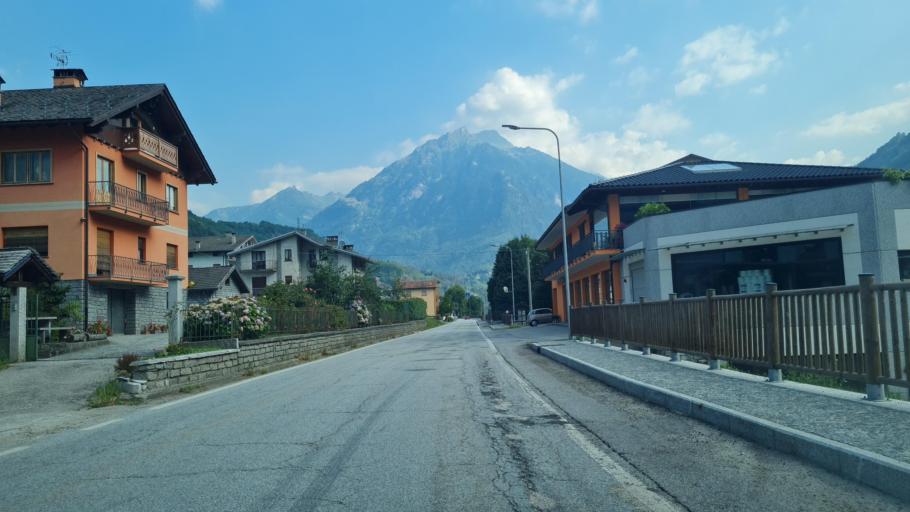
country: IT
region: Piedmont
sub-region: Provincia Verbano-Cusio-Ossola
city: Crodo
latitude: 46.2276
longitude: 8.3252
